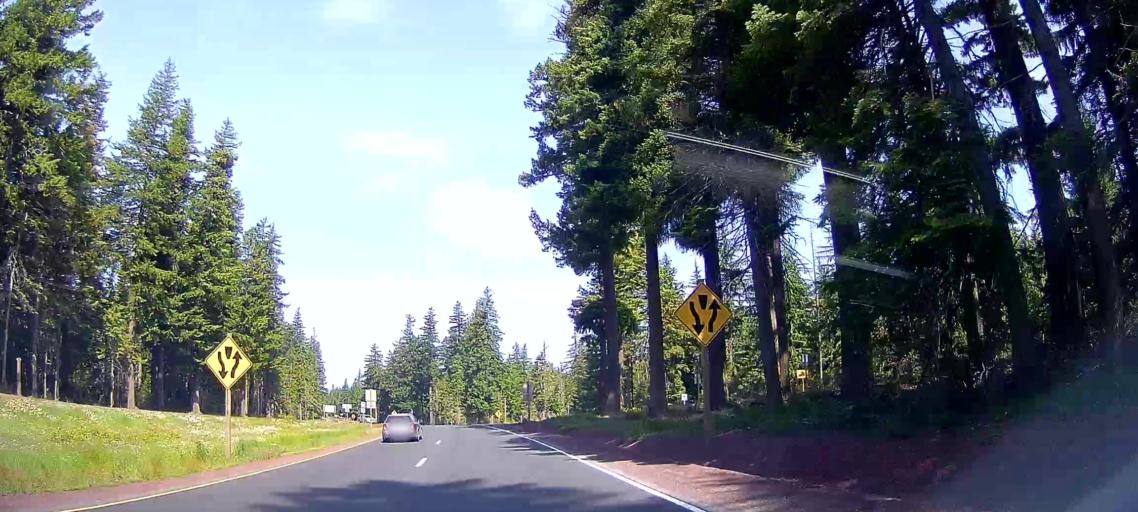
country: US
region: Oregon
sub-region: Clackamas County
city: Mount Hood Village
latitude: 45.1307
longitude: -121.6004
